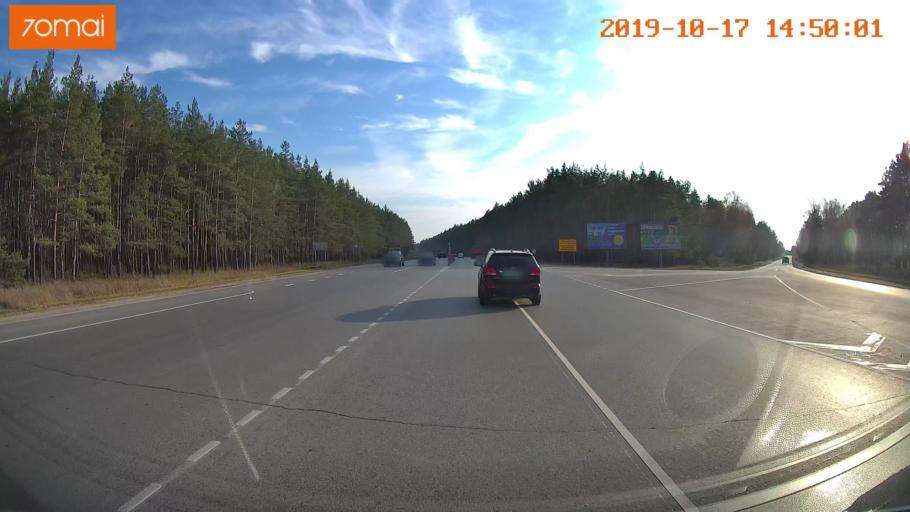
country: RU
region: Rjazan
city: Polyany
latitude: 54.7395
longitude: 39.8408
